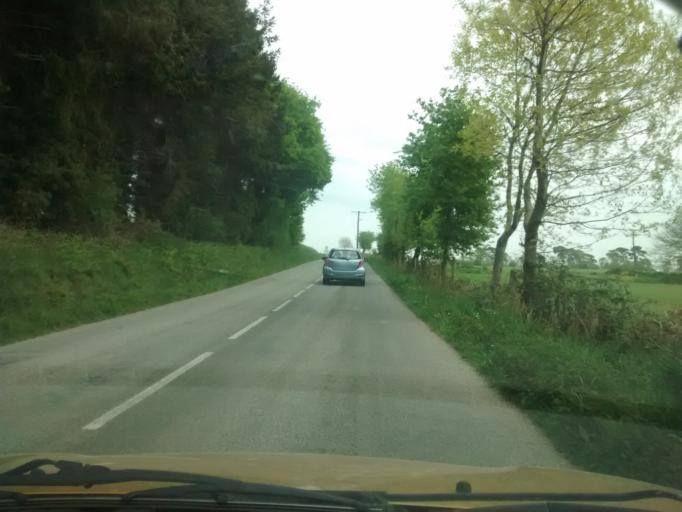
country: FR
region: Brittany
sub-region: Departement du Morbihan
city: Berric
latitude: 47.6441
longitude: -2.5044
